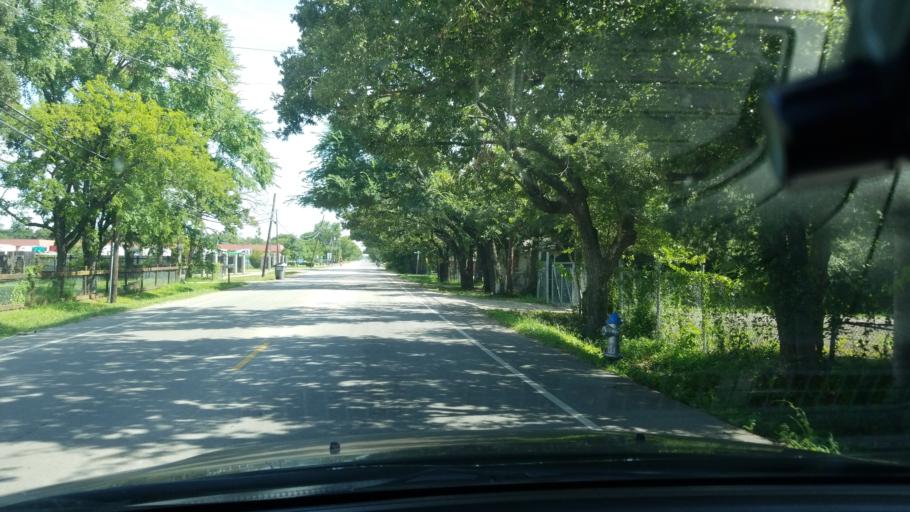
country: US
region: Texas
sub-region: Dallas County
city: Balch Springs
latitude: 32.7215
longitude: -96.6312
